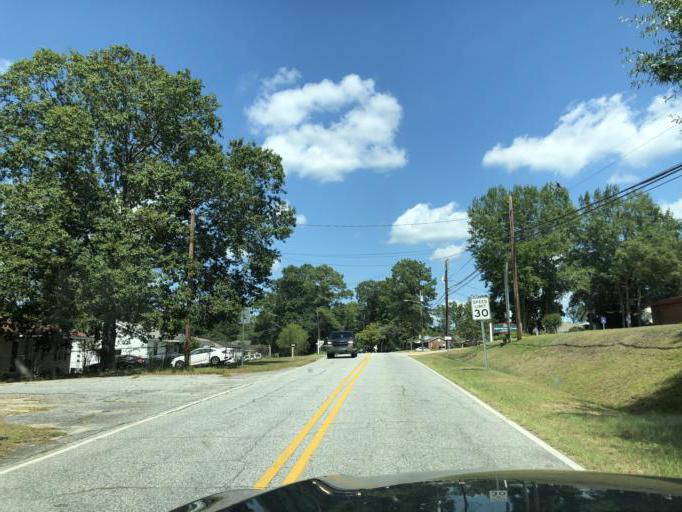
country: US
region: Georgia
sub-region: Muscogee County
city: Columbus
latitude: 32.4882
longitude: -84.9153
